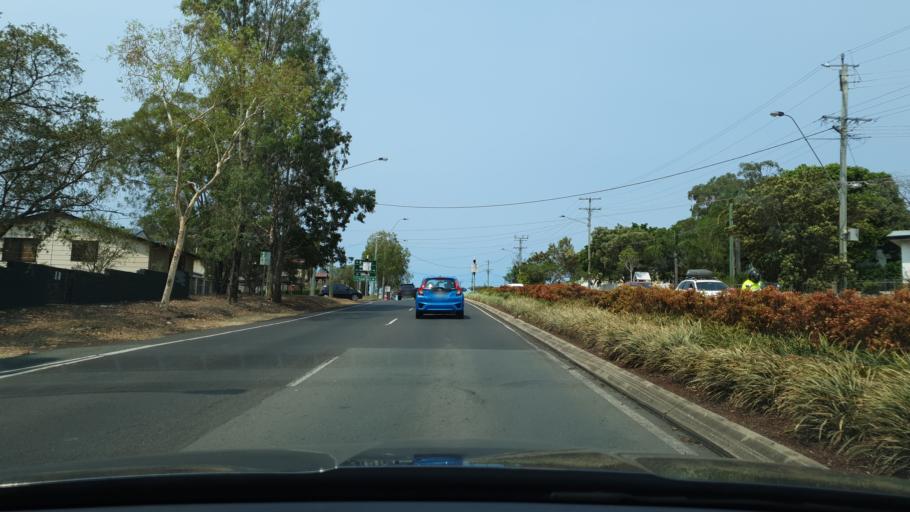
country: AU
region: Queensland
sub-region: Ipswich
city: Riverview
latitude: -27.5993
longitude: 152.8295
